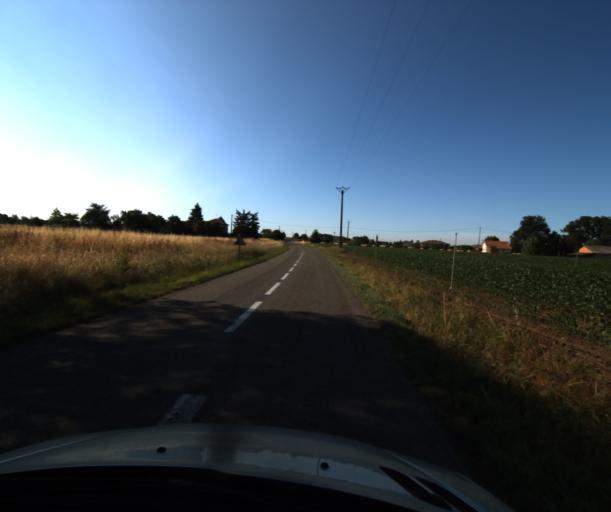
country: FR
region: Midi-Pyrenees
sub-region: Departement du Tarn-et-Garonne
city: Saint-Porquier
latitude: 44.0429
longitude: 1.2156
